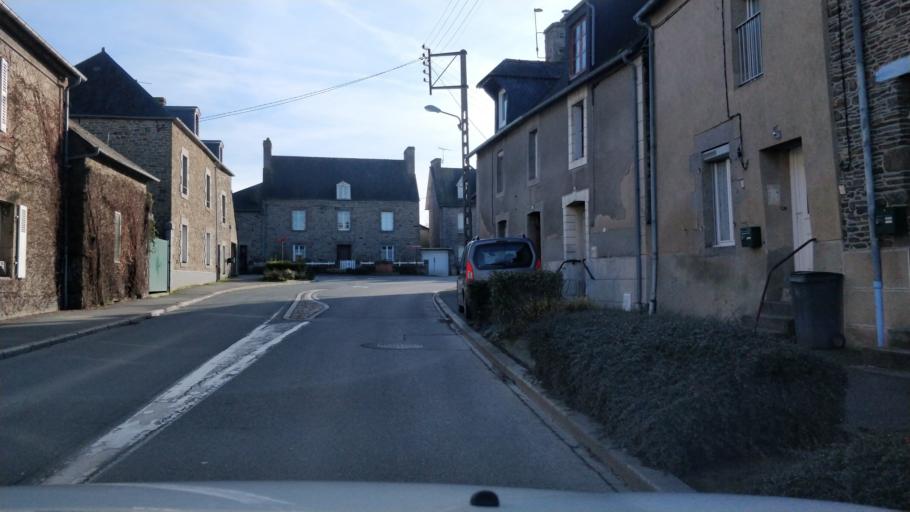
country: FR
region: Brittany
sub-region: Departement d'Ille-et-Vilaine
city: Dol-de-Bretagne
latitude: 48.5431
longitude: -1.7600
